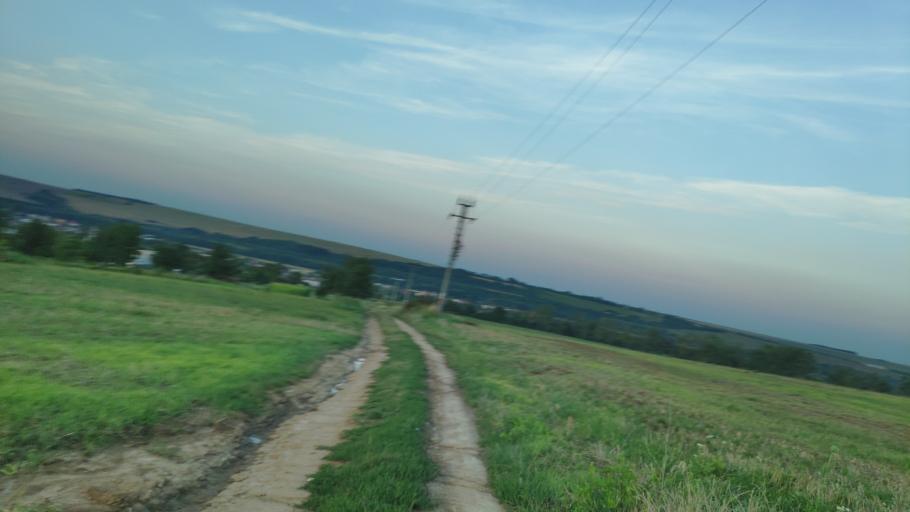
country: SK
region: Kosicky
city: Secovce
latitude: 48.5944
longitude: 21.5487
